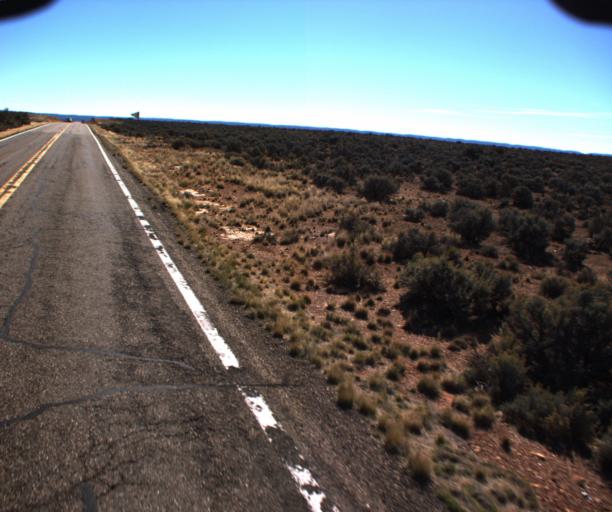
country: US
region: Arizona
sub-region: Coconino County
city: Fredonia
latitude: 36.8970
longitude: -112.3684
